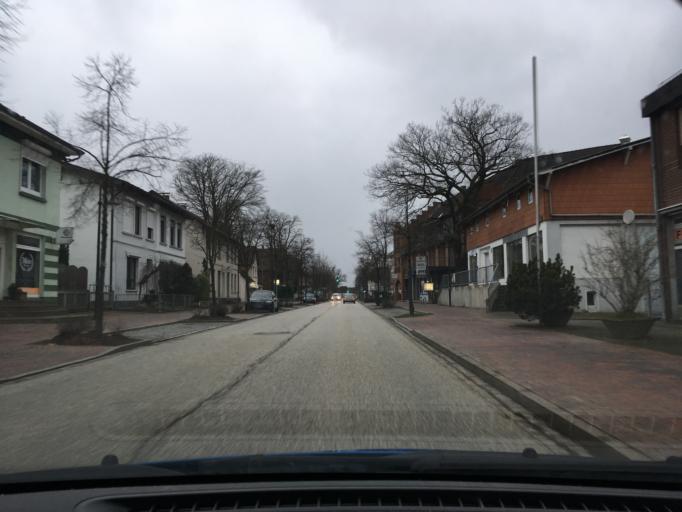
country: DE
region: Schleswig-Holstein
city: Schwarzenbek
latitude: 53.5014
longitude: 10.4848
